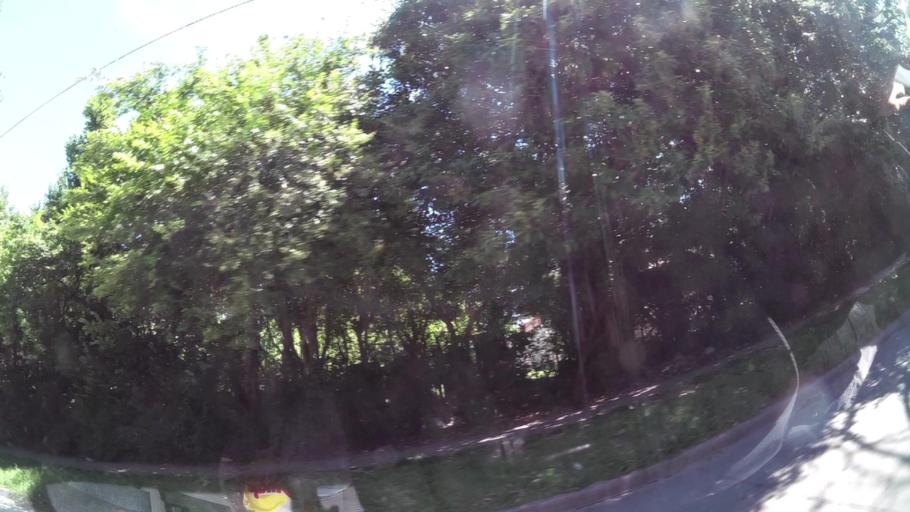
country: AR
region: Buenos Aires
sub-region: Partido de Tigre
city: Tigre
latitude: -34.4895
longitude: -58.6537
